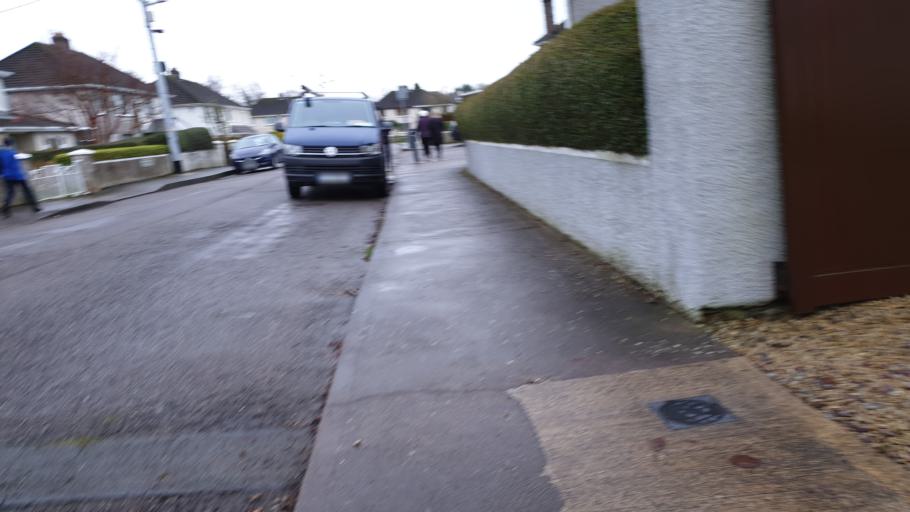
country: IE
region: Munster
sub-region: County Cork
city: Cork
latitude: 51.8893
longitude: -8.4209
